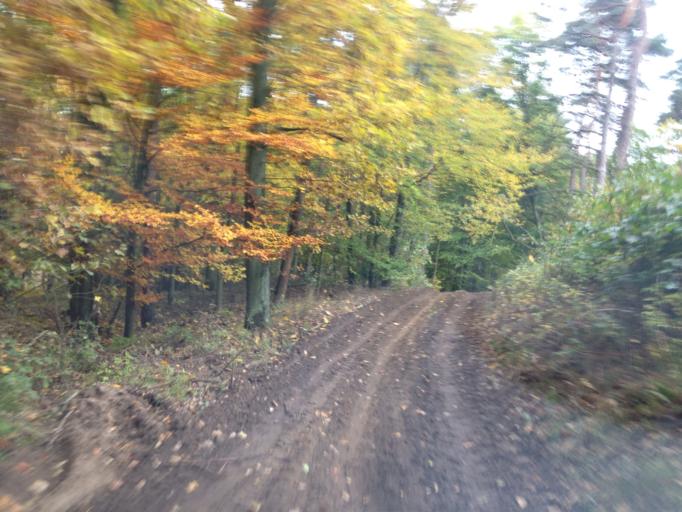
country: PL
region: Kujawsko-Pomorskie
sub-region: Powiat brodnicki
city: Gorzno
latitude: 53.2478
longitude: 19.6822
